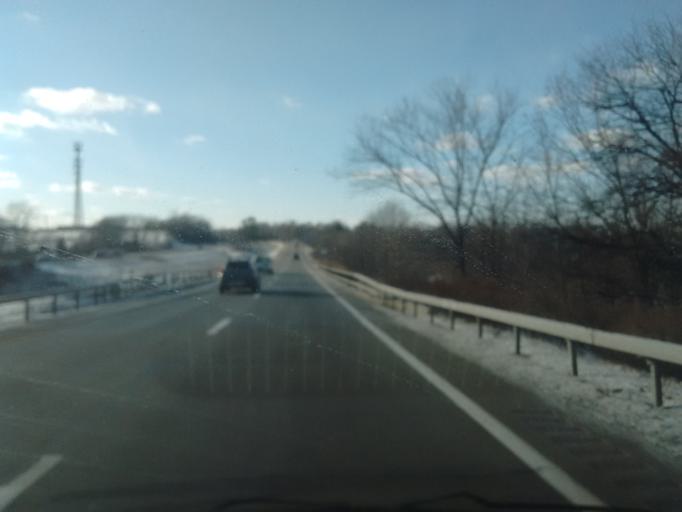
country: US
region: New York
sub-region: Dutchess County
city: Beacon
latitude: 41.5302
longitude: -73.9417
